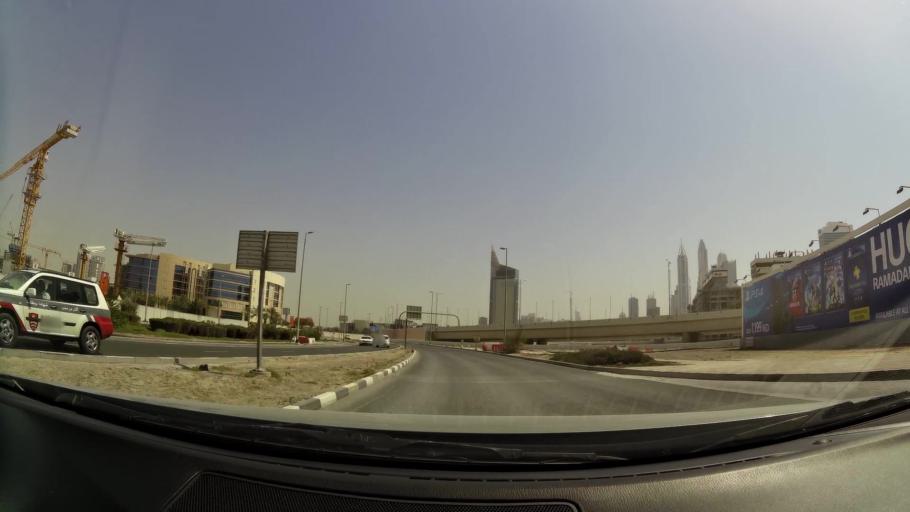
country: AE
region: Dubai
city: Dubai
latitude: 25.1004
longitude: 55.1628
